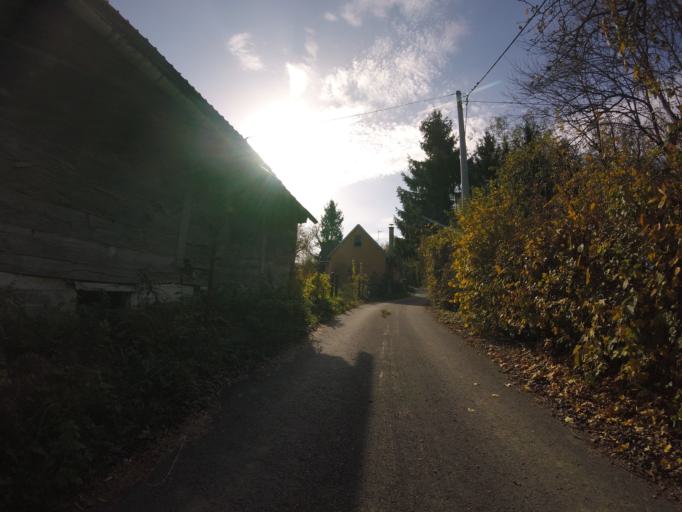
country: HR
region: Zagrebacka
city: Lukavec
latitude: 45.6259
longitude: 16.0140
